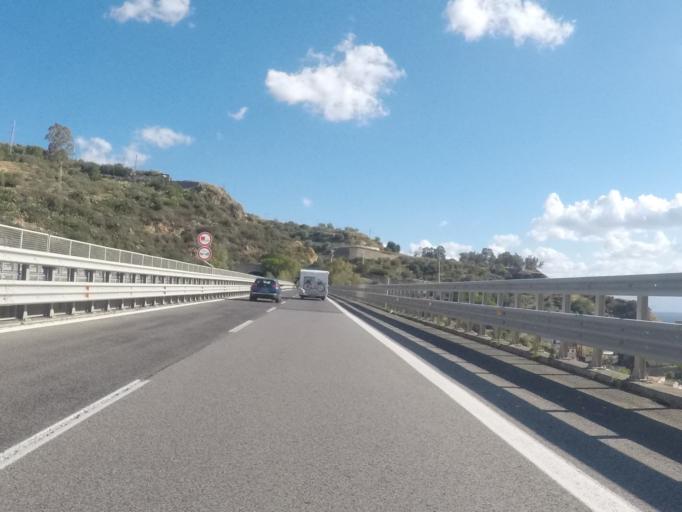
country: IT
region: Sicily
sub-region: Messina
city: Ali Terme
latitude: 38.0084
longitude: 15.4242
